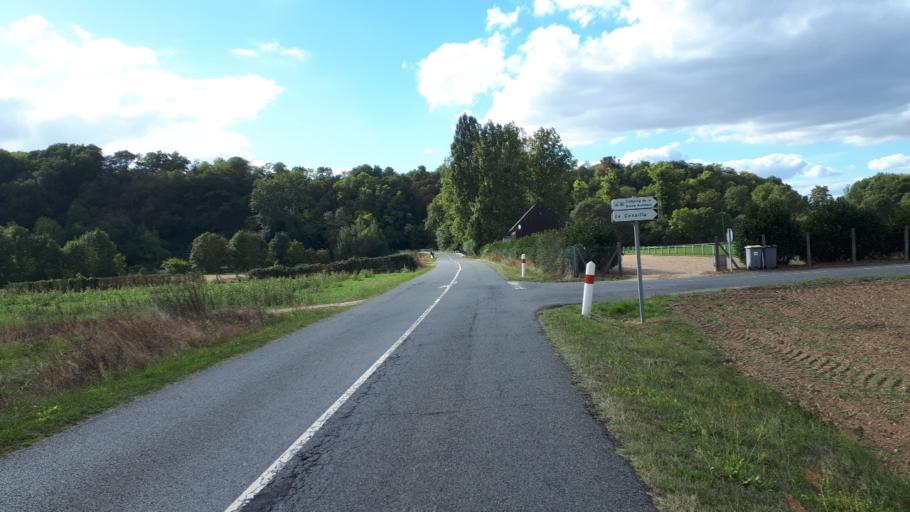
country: FR
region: Centre
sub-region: Departement du Loir-et-Cher
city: Villiers-sur-Loir
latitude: 47.7935
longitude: 0.9567
